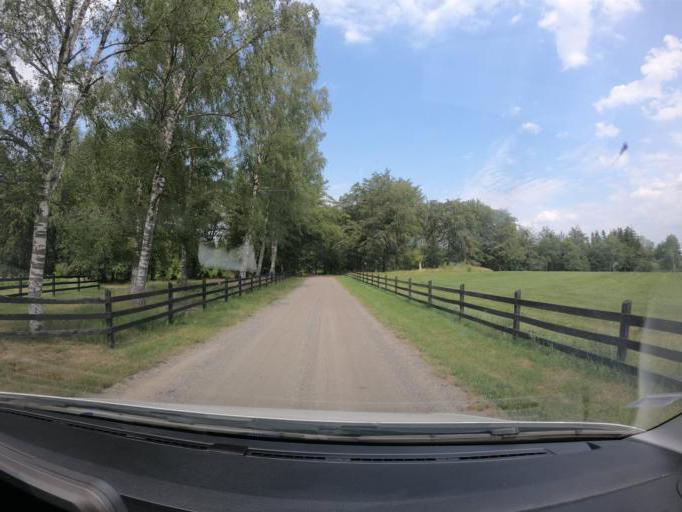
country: SE
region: Skane
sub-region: Hassleholms Kommun
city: Bjarnum
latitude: 56.2393
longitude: 13.6009
